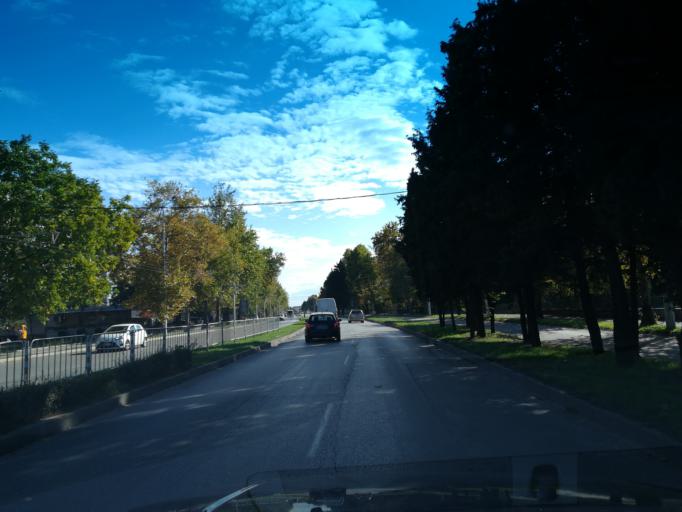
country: BG
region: Stara Zagora
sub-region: Obshtina Stara Zagora
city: Stara Zagora
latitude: 42.4081
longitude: 25.6403
